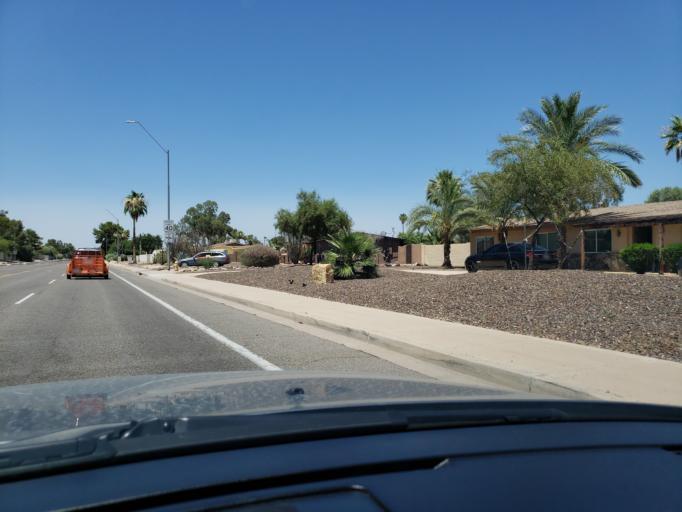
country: US
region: Arizona
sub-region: Maricopa County
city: Paradise Valley
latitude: 33.5983
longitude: -111.9433
